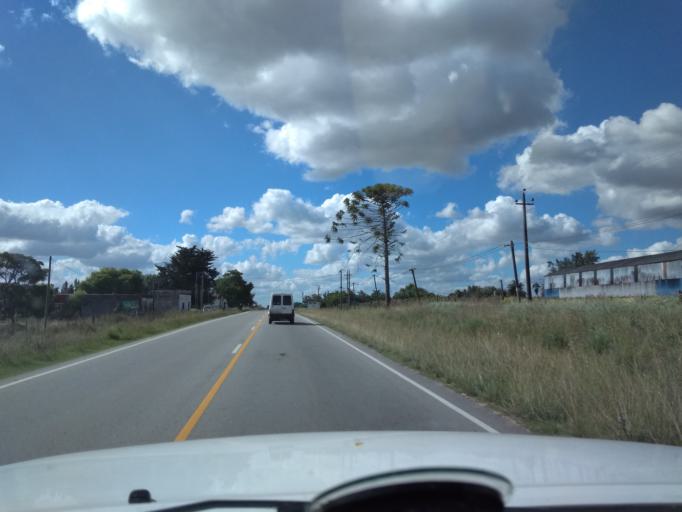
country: UY
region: Canelones
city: Sauce
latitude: -34.6879
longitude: -56.0539
